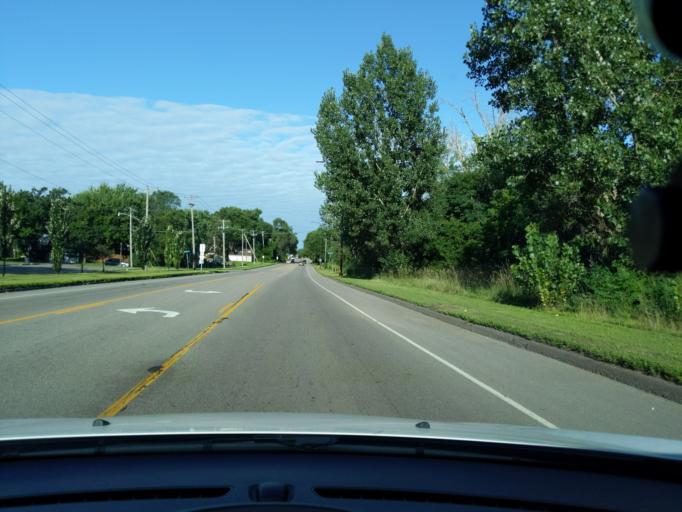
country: US
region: Minnesota
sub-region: Ramsey County
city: Falcon Heights
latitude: 44.9689
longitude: -93.1759
